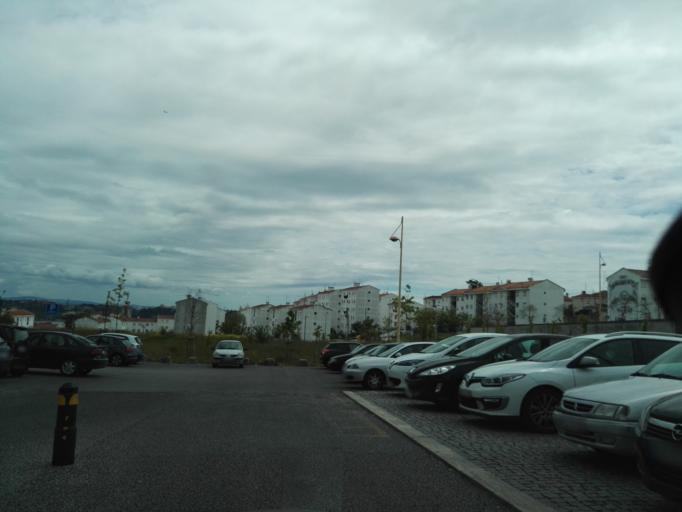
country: PT
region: Lisbon
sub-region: Oeiras
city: Alges
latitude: 38.7129
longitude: -9.1982
